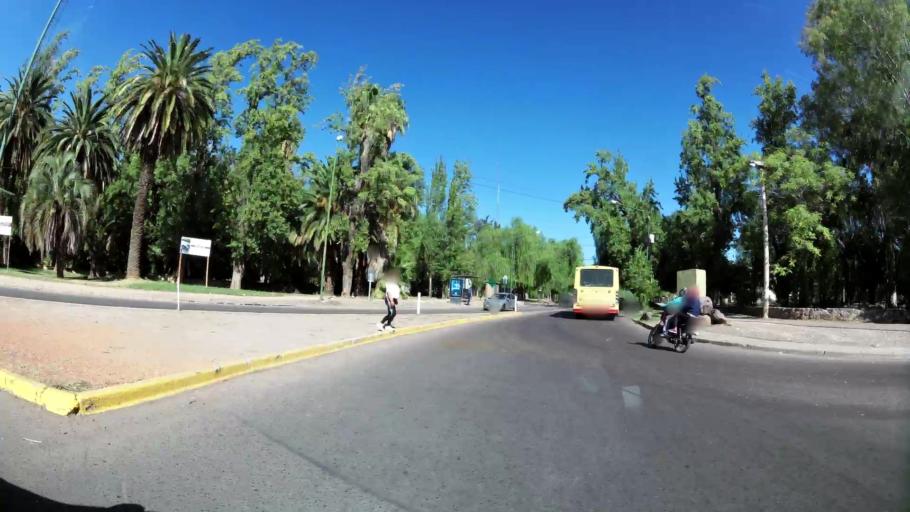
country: AR
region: Mendoza
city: Mendoza
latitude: -32.8843
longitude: -68.8735
